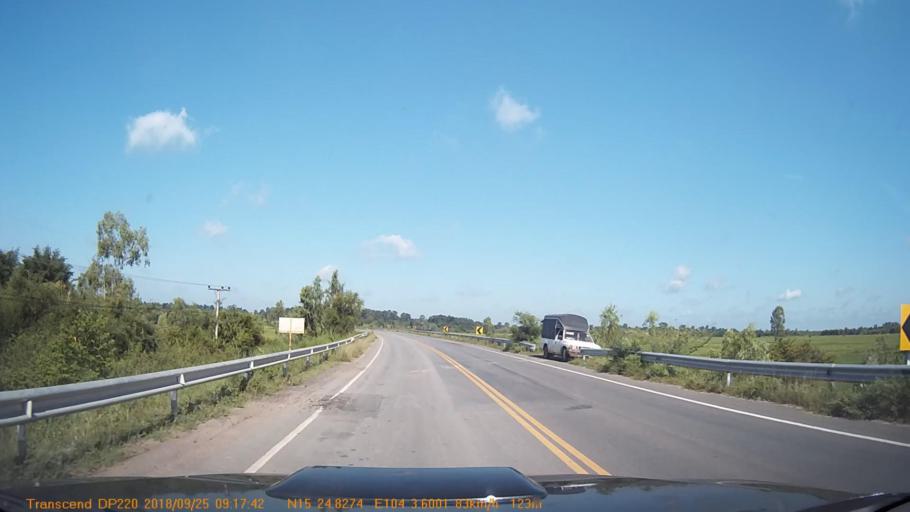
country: TH
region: Sisaket
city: Sila Lat
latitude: 15.4138
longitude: 104.0601
